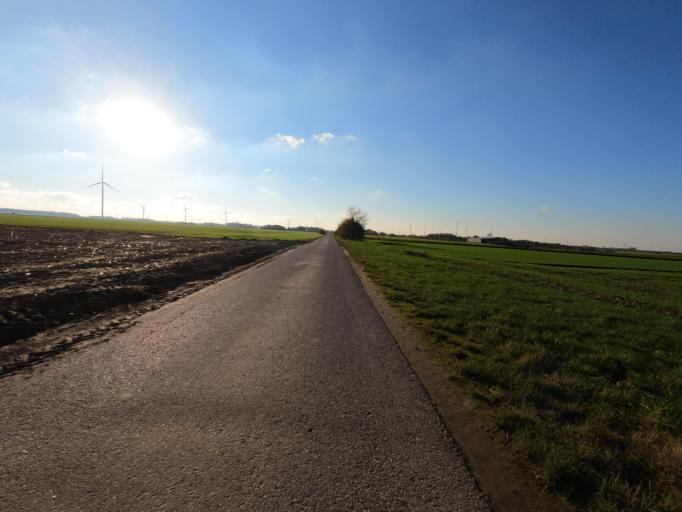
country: DE
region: North Rhine-Westphalia
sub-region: Regierungsbezirk Koln
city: Heinsberg
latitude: 51.0237
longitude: 6.1528
